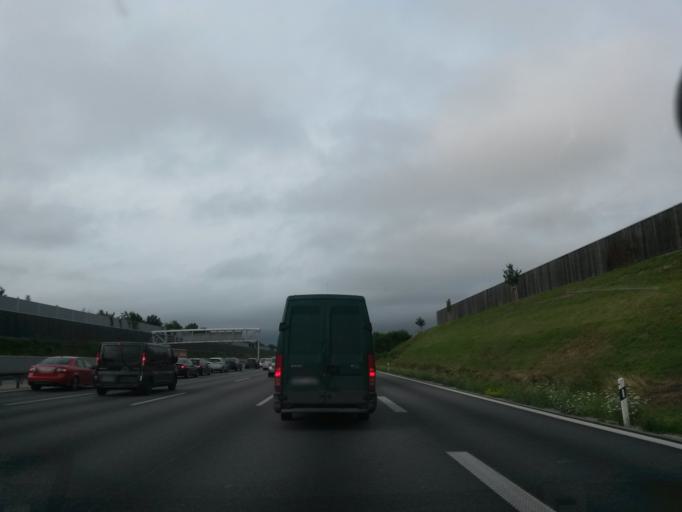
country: DE
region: Bavaria
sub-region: Upper Bavaria
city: Garching bei Munchen
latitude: 48.2485
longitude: 11.6428
